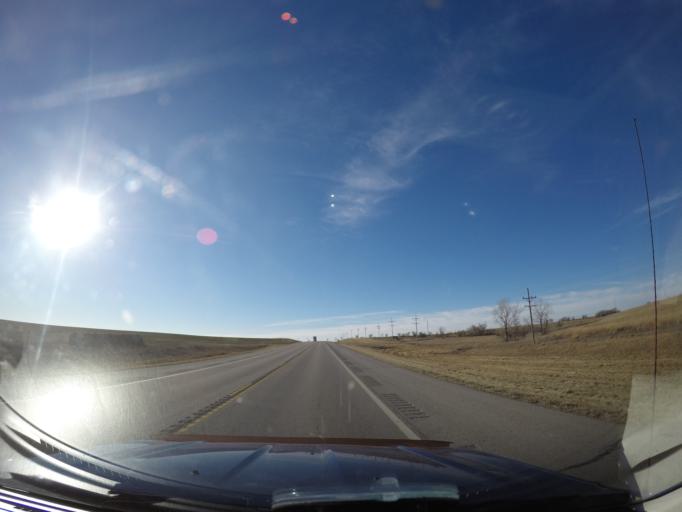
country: US
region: Kansas
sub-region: Marion County
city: Hillsboro
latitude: 38.3624
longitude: -97.3284
